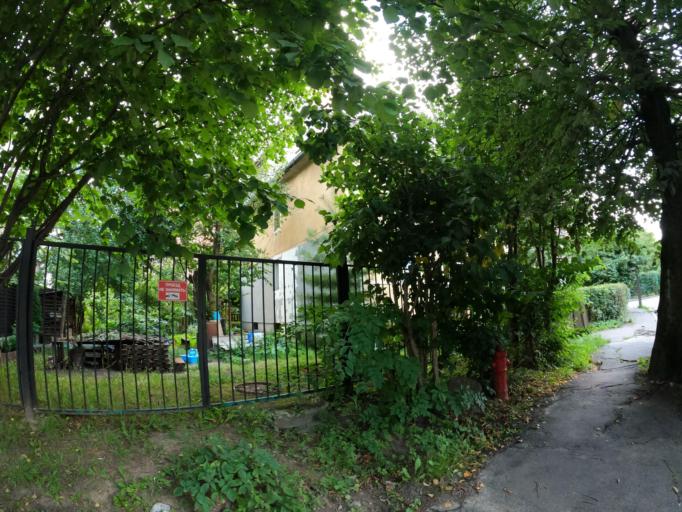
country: RU
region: Kaliningrad
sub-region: Gorod Kaliningrad
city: Kaliningrad
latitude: 54.7308
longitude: 20.4727
